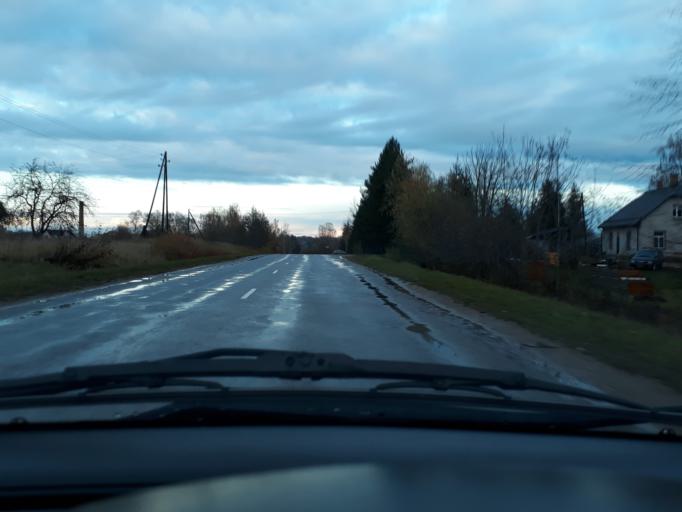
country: LV
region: Dobeles Rajons
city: Dobele
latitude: 56.6182
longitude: 23.2617
